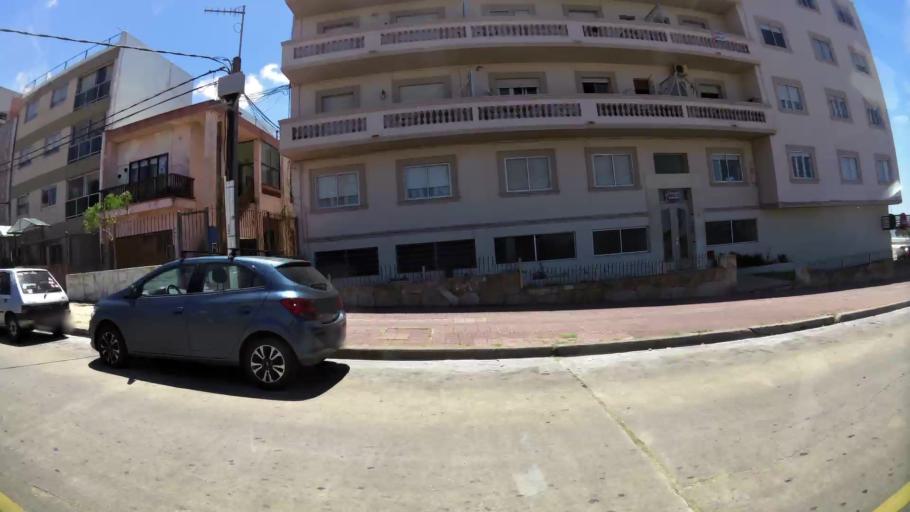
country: UY
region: Montevideo
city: Montevideo
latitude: -34.8977
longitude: -56.1199
